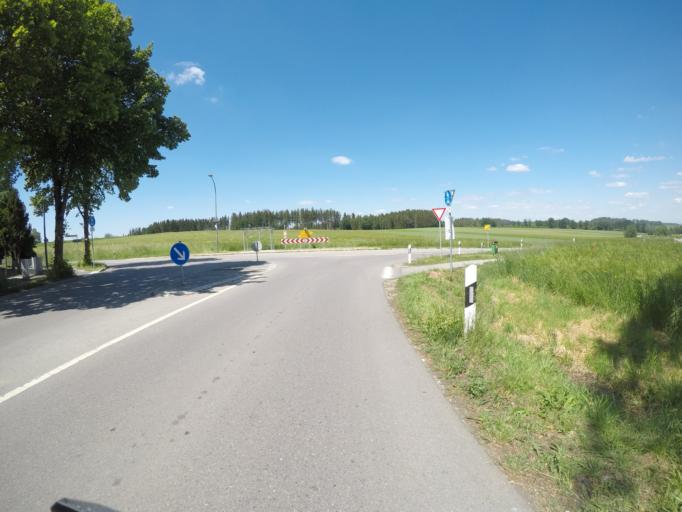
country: DE
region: Bavaria
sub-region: Lower Bavaria
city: Kumhausen
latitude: 48.4900
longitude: 12.1905
